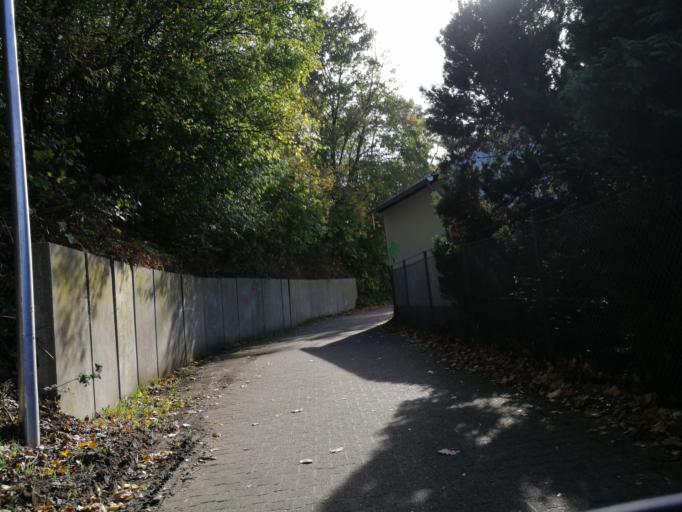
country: DE
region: North Rhine-Westphalia
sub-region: Regierungsbezirk Dusseldorf
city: Dusseldorf
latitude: 51.1883
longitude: 6.7752
